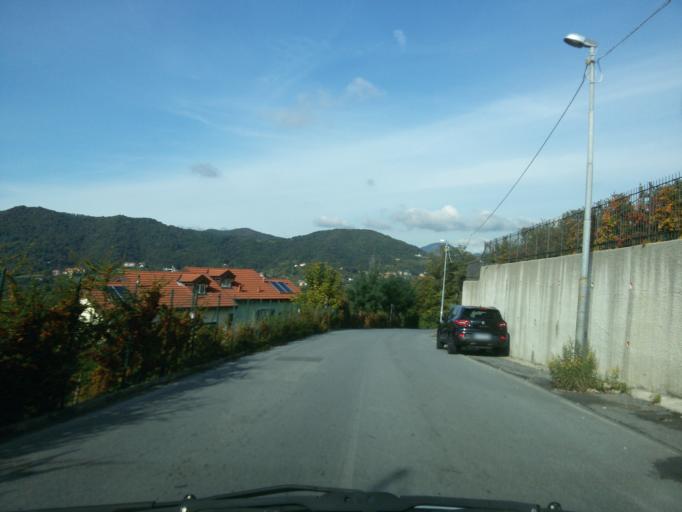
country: IT
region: Liguria
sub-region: Provincia di Genova
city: Piccarello
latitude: 44.4750
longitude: 8.9608
